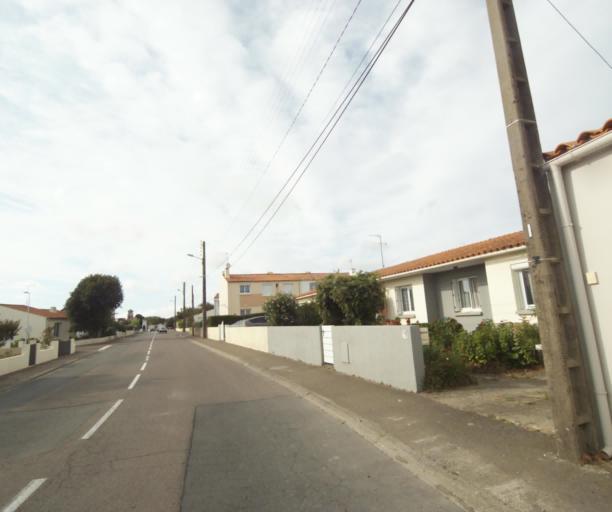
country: FR
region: Pays de la Loire
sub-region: Departement de la Vendee
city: Chateau-d'Olonne
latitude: 46.5013
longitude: -1.7331
